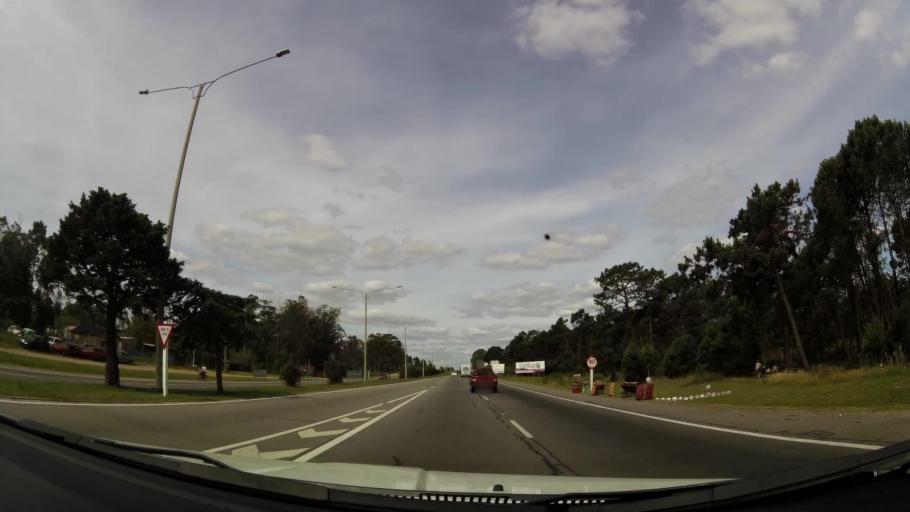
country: UY
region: Canelones
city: Empalme Olmos
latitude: -34.7833
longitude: -55.8846
